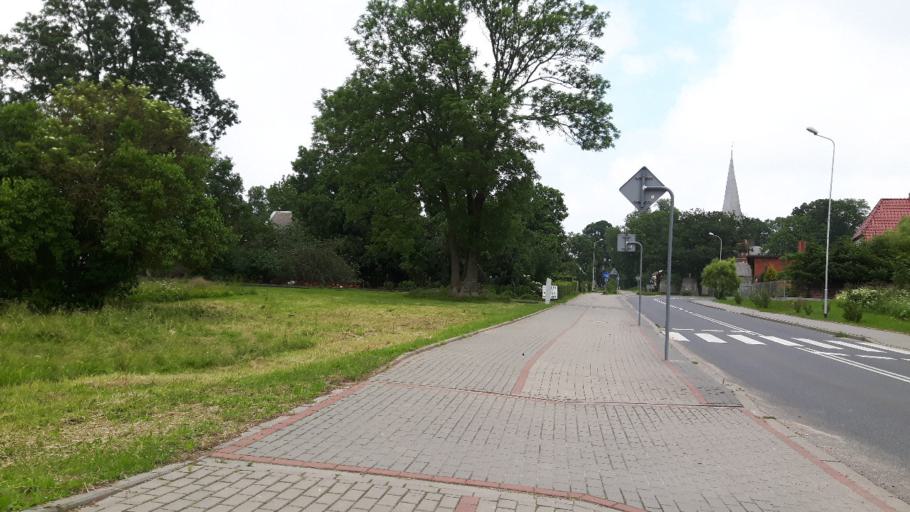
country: PL
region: West Pomeranian Voivodeship
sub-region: Powiat koszalinski
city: Sianow
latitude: 54.2944
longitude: 16.2742
